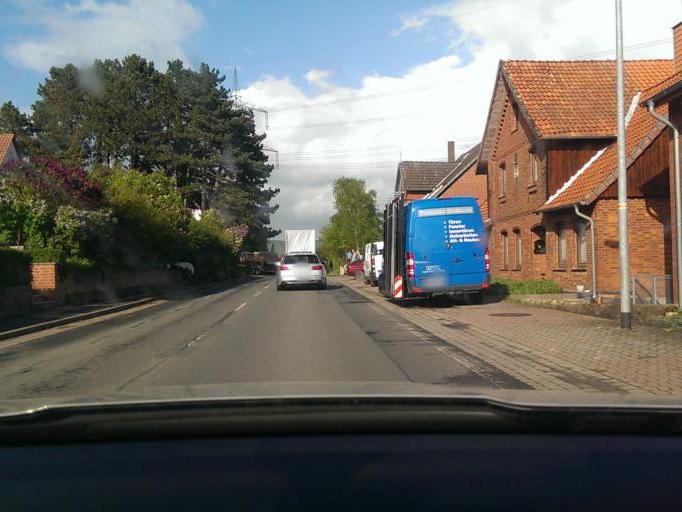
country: DE
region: Lower Saxony
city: Pohle
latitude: 52.2667
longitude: 9.3475
